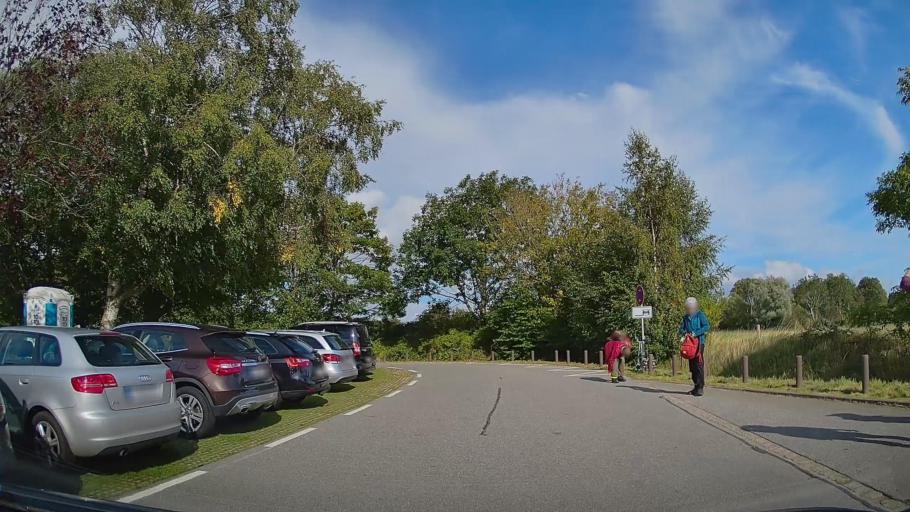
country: DK
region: South Denmark
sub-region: Sonderborg Kommune
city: Grasten
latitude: 54.8714
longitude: 9.6003
